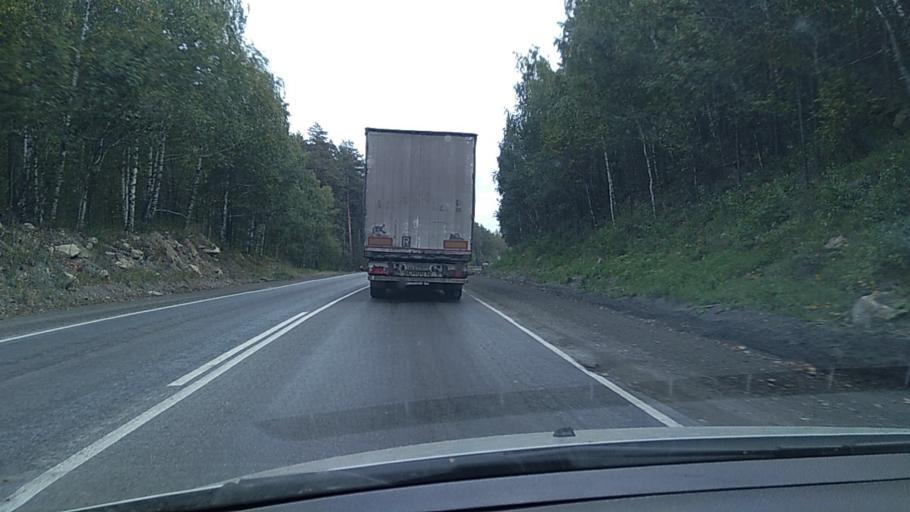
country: RU
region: Chelyabinsk
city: Miass
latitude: 54.9445
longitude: 60.1082
